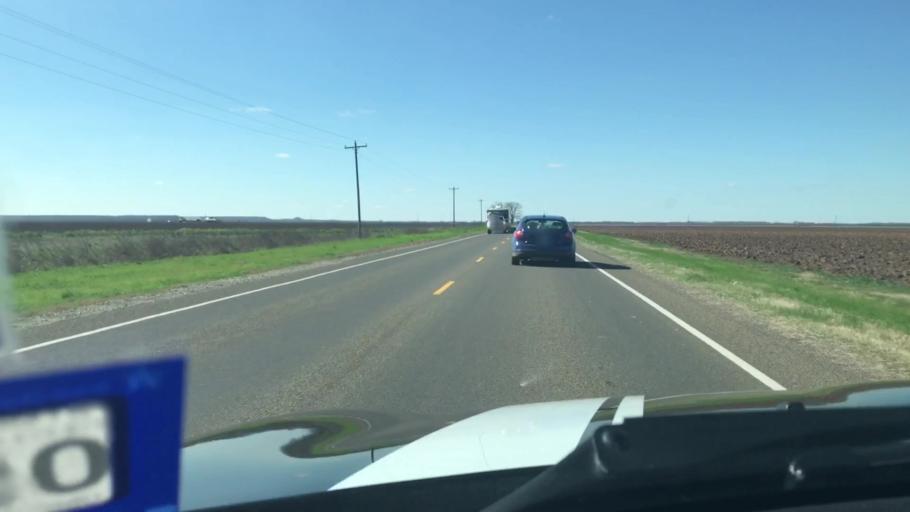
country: US
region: Texas
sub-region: Robertson County
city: Hearne
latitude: 30.8759
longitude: -96.6514
